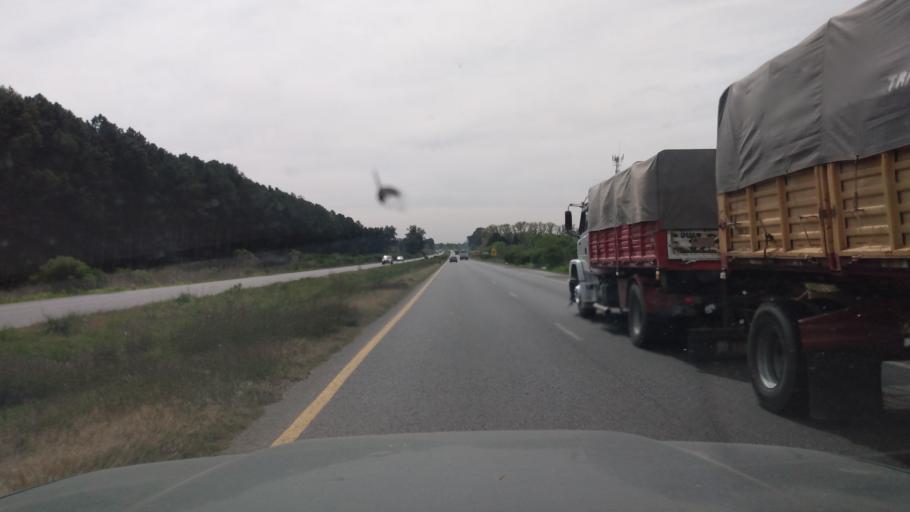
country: AR
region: Buenos Aires
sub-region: Partido de Lujan
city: Lujan
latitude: -34.4643
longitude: -59.0637
